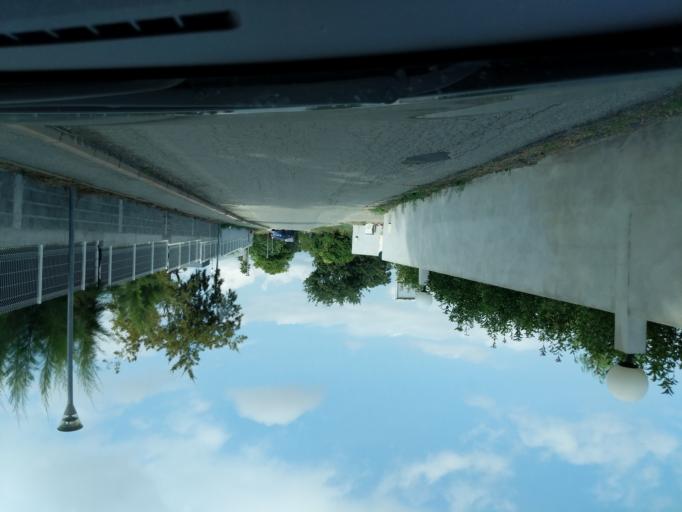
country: FR
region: Corsica
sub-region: Departement de la Haute-Corse
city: Ghisonaccia
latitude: 42.0019
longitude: 9.4425
